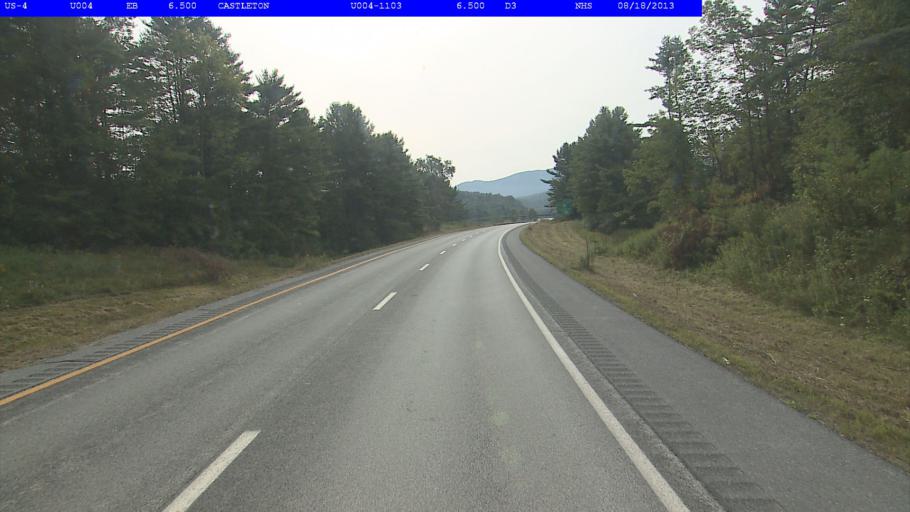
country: US
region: Vermont
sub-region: Rutland County
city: Castleton
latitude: 43.6222
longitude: -73.1887
